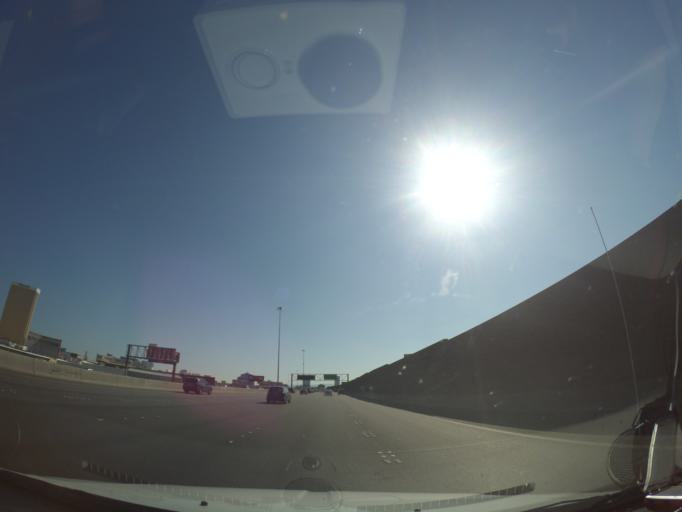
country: US
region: Nevada
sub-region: Clark County
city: Paradise
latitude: 36.1388
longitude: -115.1763
